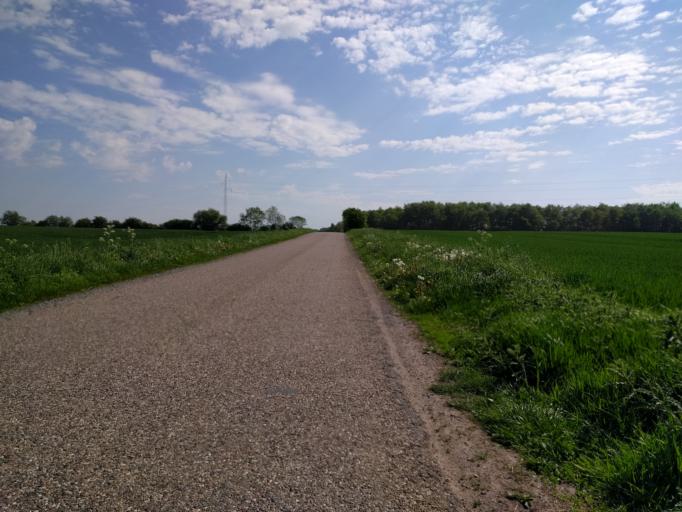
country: DK
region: South Denmark
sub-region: Kerteminde Kommune
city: Munkebo
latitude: 55.4694
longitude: 10.5917
